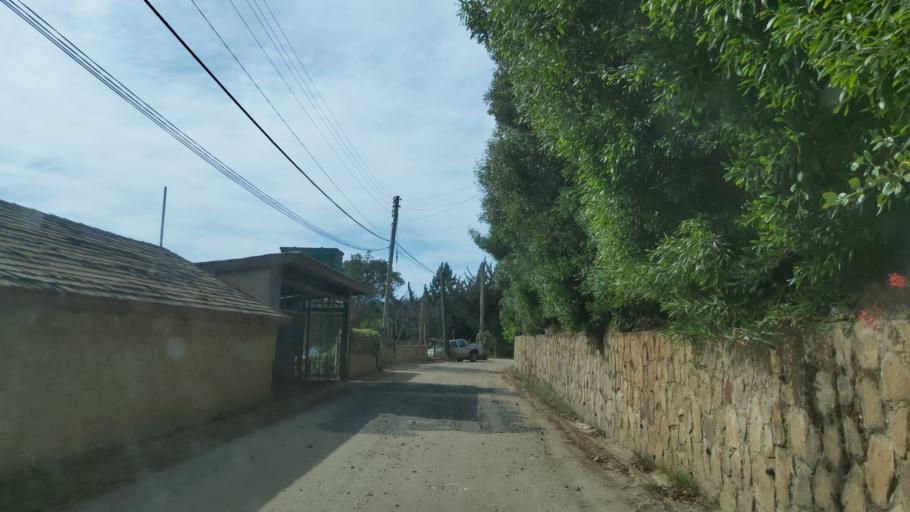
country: CL
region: Maule
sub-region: Provincia de Talca
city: Constitucion
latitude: -34.8412
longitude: -72.0414
